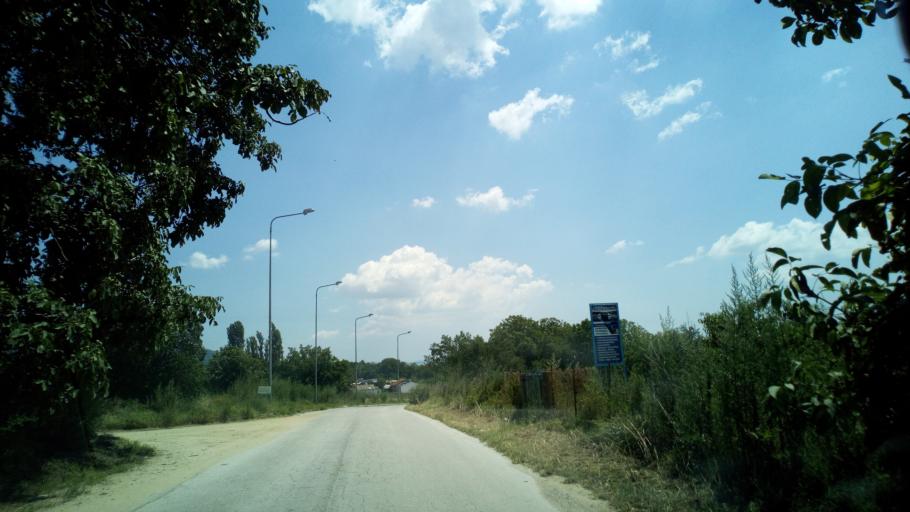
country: GR
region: Central Macedonia
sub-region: Nomos Thessalonikis
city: Sochos
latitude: 40.8121
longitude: 23.3615
